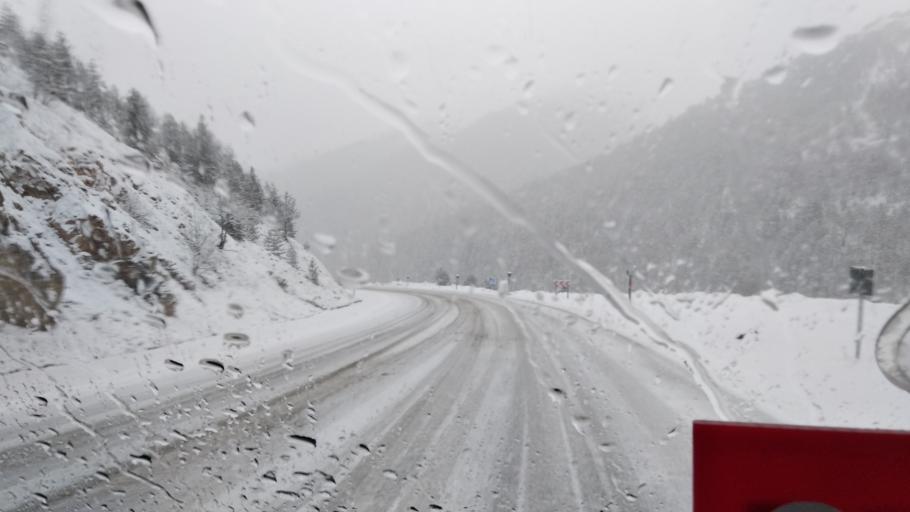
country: TR
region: Gumushane
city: Yaglidere
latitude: 40.6578
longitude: 39.4115
